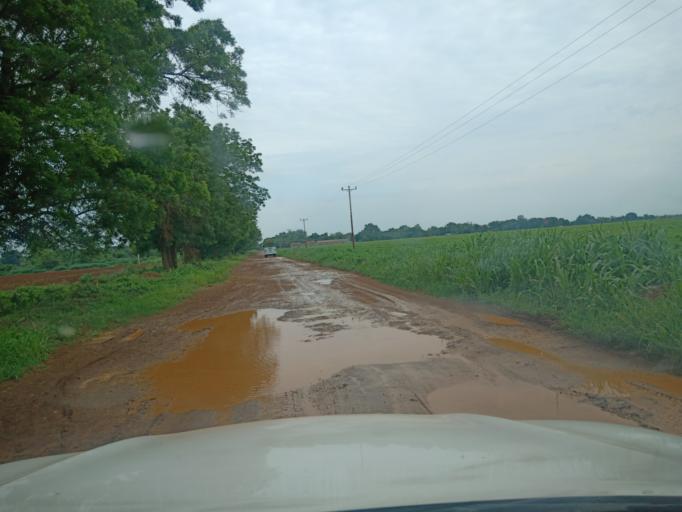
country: ET
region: Gambela
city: Gambela
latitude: 7.8962
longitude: 34.5489
